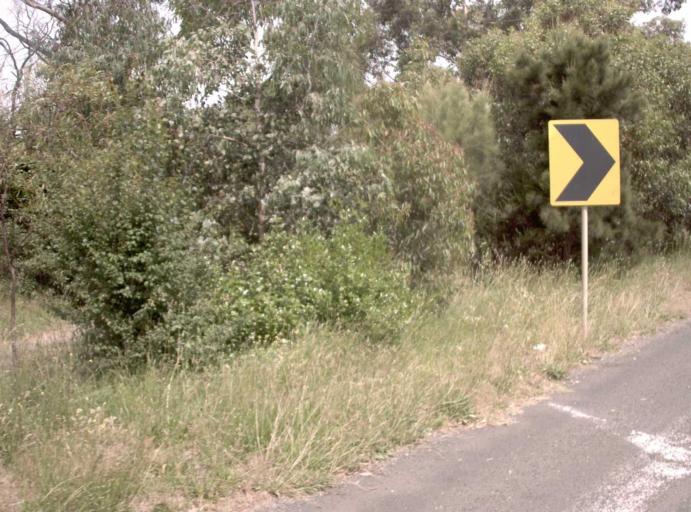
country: AU
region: Victoria
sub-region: Mornington Peninsula
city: Baxter
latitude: -38.1883
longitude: 145.1412
